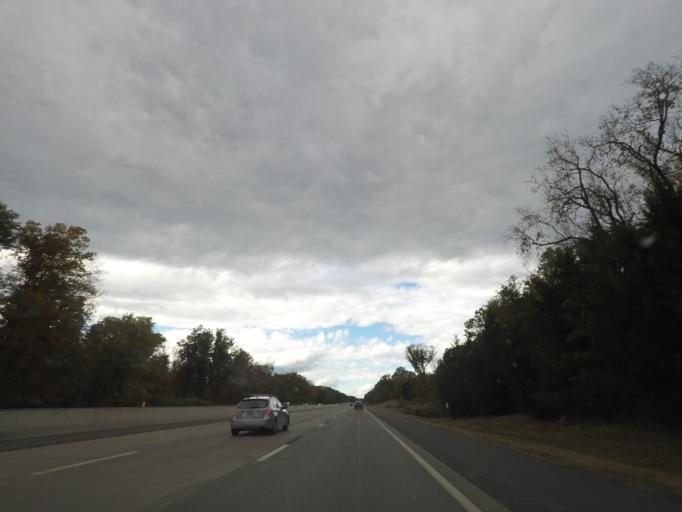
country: US
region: New York
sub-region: Albany County
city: McKownville
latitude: 42.6659
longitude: -73.8329
